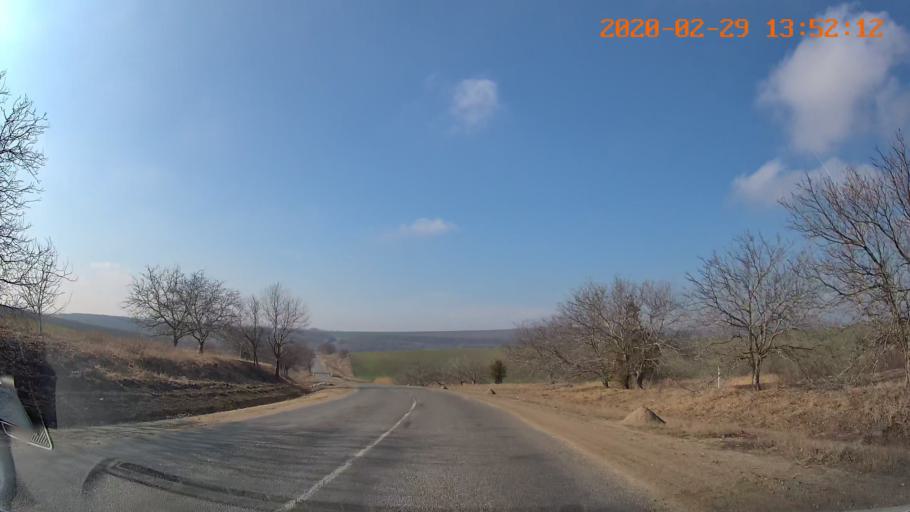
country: MD
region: Floresti
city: Leninskiy
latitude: 47.8449
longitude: 28.4523
